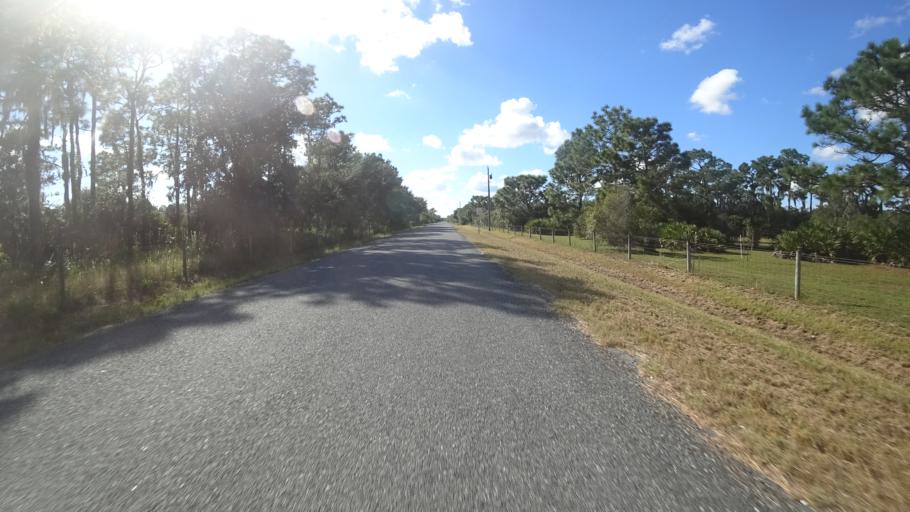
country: US
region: Florida
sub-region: Sarasota County
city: Fruitville
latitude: 27.4053
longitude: -82.2919
